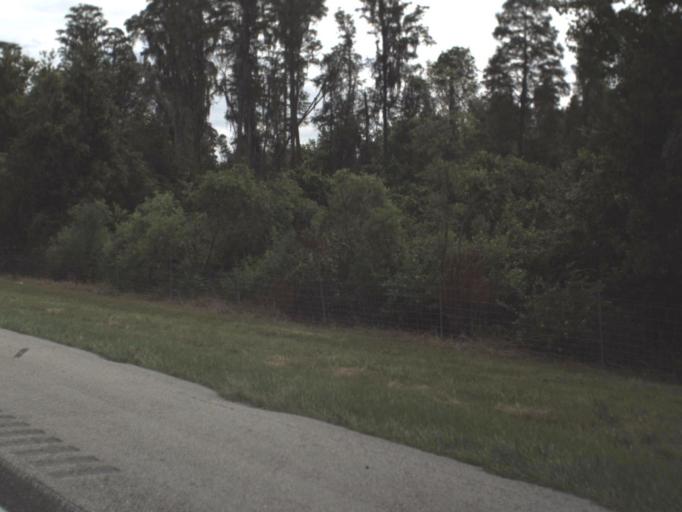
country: US
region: Florida
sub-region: Polk County
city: Polk City
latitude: 28.1793
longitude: -81.7503
